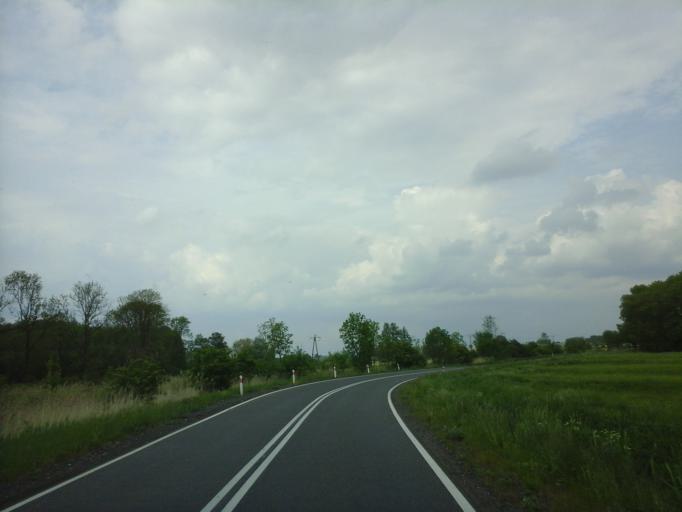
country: PL
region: West Pomeranian Voivodeship
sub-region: Powiat choszczenski
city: Pelczyce
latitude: 53.1148
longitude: 15.3448
